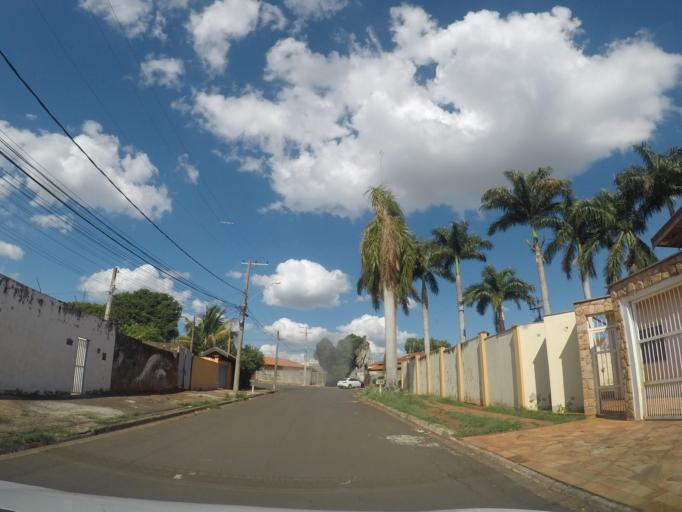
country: BR
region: Sao Paulo
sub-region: Sumare
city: Sumare
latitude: -22.8342
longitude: -47.2777
